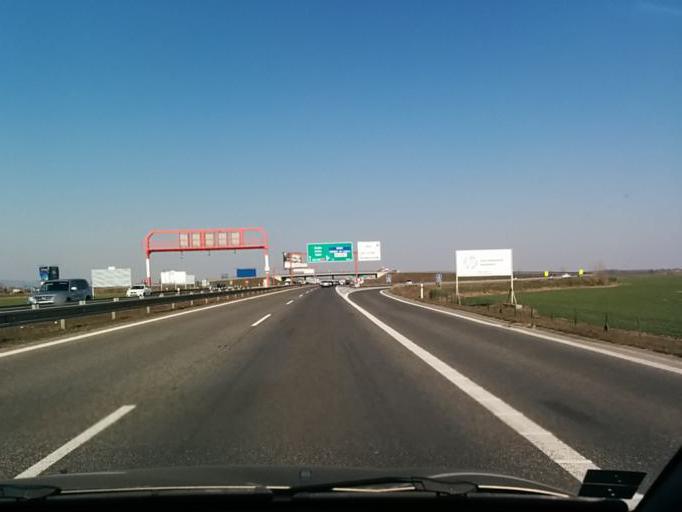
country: SK
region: Bratislavsky
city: Svaty Jur
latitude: 48.1836
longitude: 17.1982
